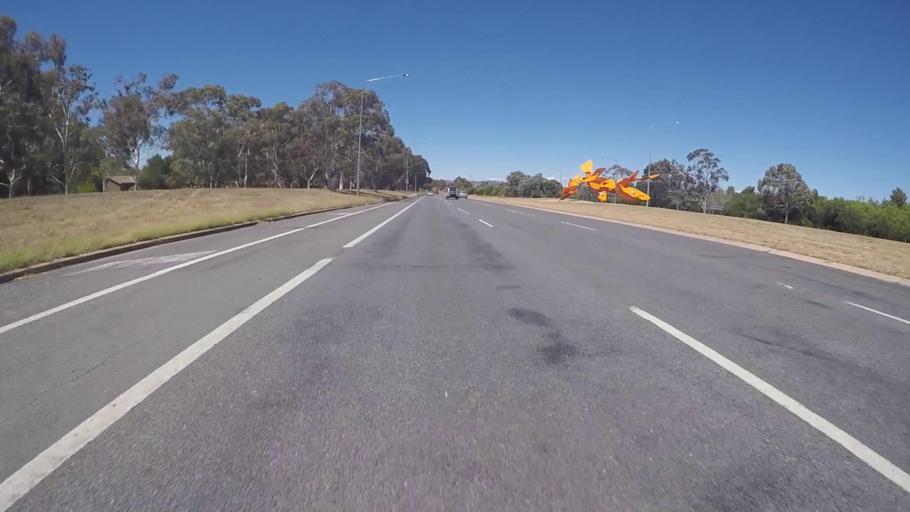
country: AU
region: Australian Capital Territory
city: Macarthur
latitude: -35.3865
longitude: 149.0624
